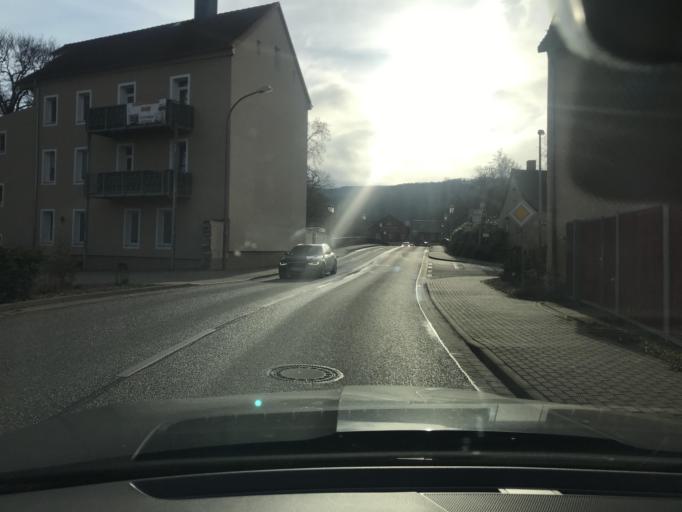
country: DE
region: Saxony-Anhalt
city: Thale
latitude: 51.7553
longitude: 11.0458
